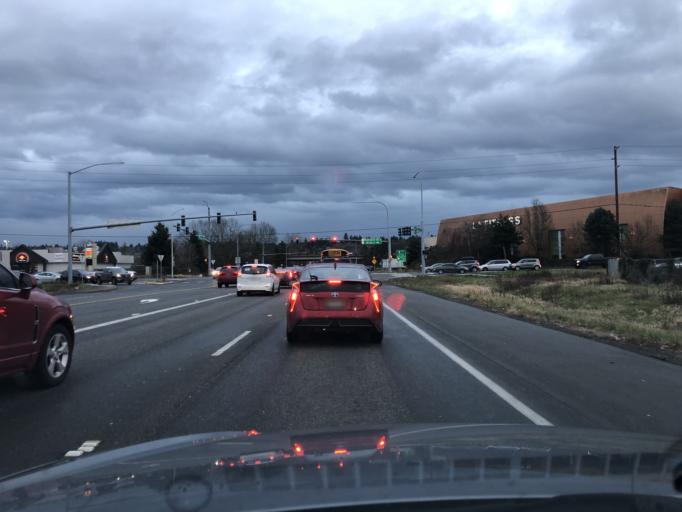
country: US
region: Washington
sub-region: King County
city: Kent
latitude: 47.3778
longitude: -122.2483
